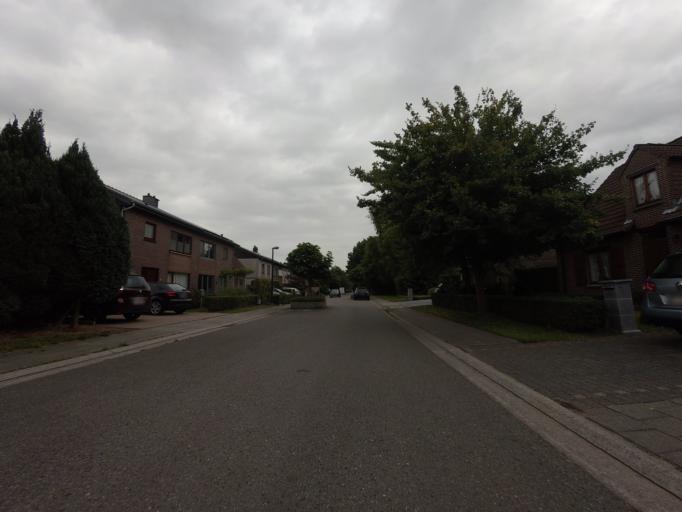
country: BE
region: Flanders
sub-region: Provincie Vlaams-Brabant
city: Meise
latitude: 50.9566
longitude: 4.3367
